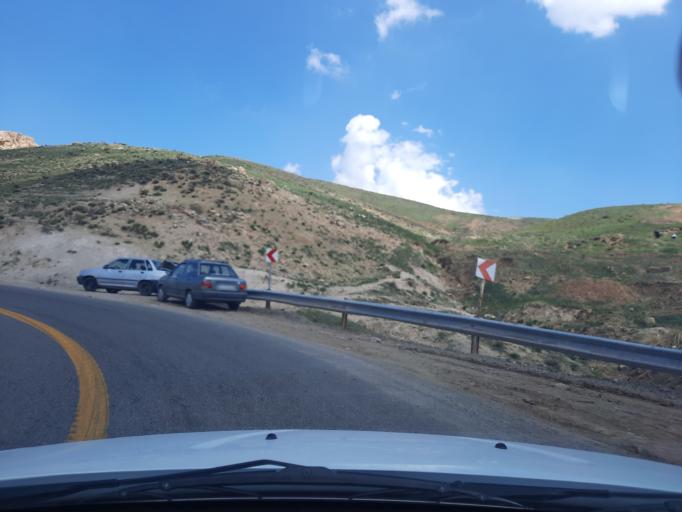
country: IR
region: Qazvin
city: Qazvin
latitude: 36.3867
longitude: 50.2111
